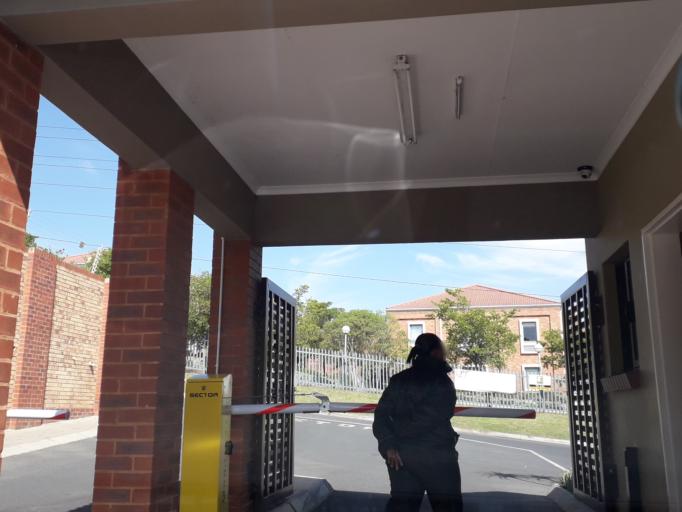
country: ZA
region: Gauteng
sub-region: West Rand District Municipality
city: Muldersdriseloop
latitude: -26.0634
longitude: 27.9712
